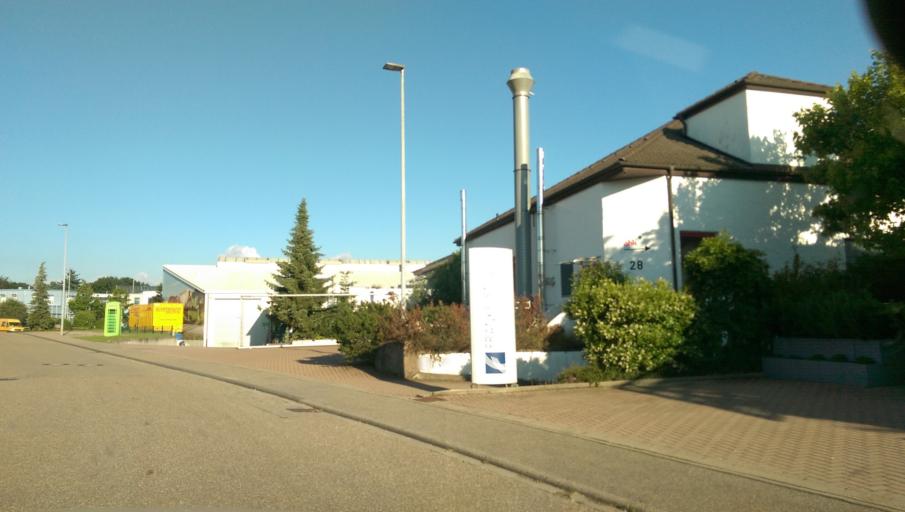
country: DE
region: Baden-Wuerttemberg
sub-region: Karlsruhe Region
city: Dobel
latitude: 48.8437
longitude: 8.5178
